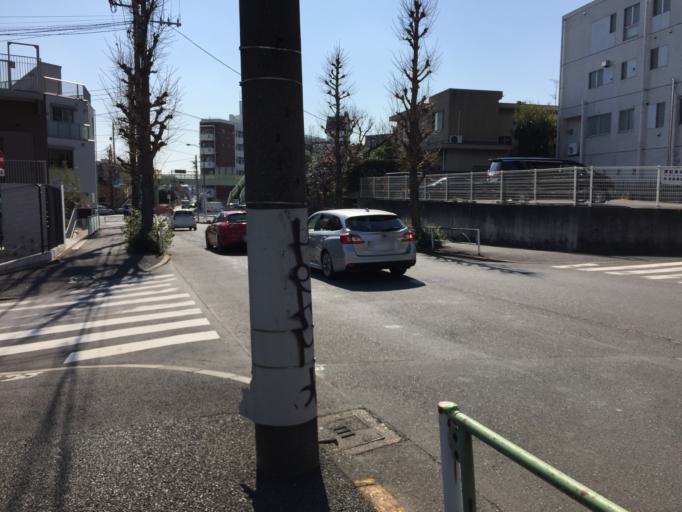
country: JP
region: Tokyo
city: Tokyo
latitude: 35.6120
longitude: 139.6526
